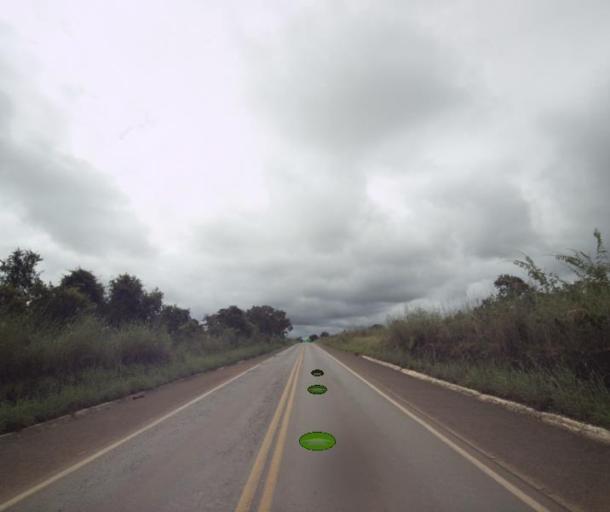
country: BR
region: Goias
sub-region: Uruacu
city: Uruacu
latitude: -14.7190
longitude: -49.0831
